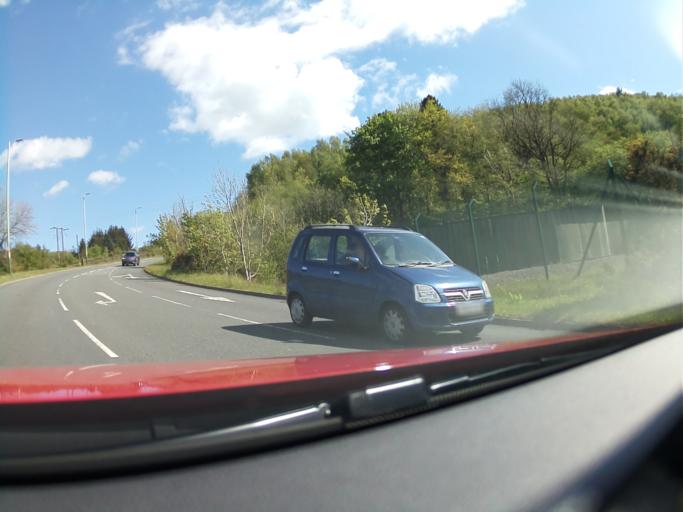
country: GB
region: Wales
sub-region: Caerphilly County Borough
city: Caerphilly
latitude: 51.5646
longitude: -3.2318
